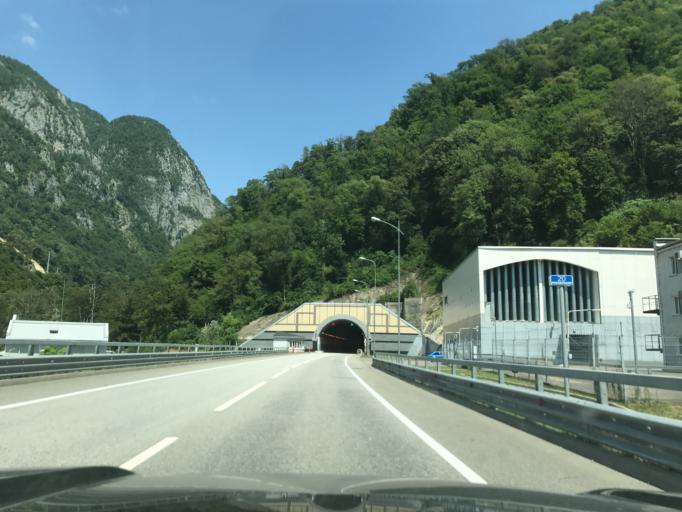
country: RU
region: Krasnodarskiy
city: Vysokoye
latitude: 43.5894
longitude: 40.0161
